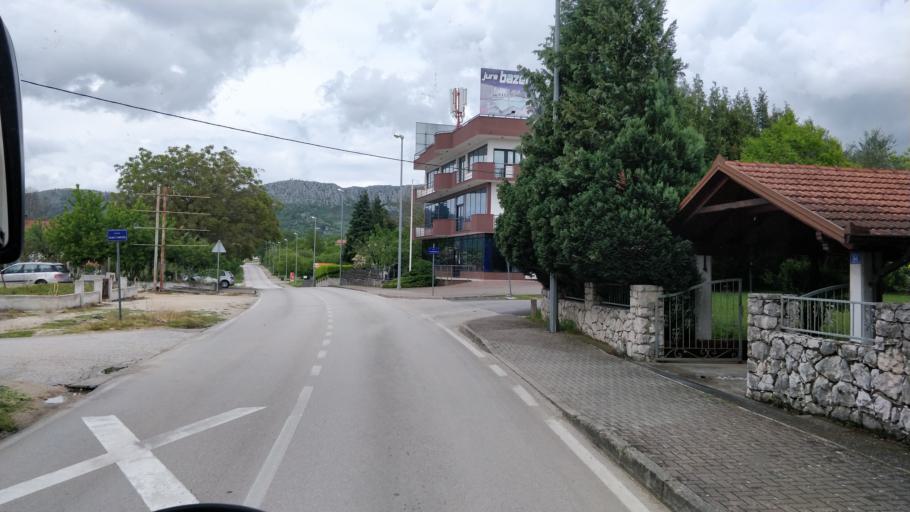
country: BA
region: Federation of Bosnia and Herzegovina
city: Ljubuski
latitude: 43.1845
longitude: 17.5283
